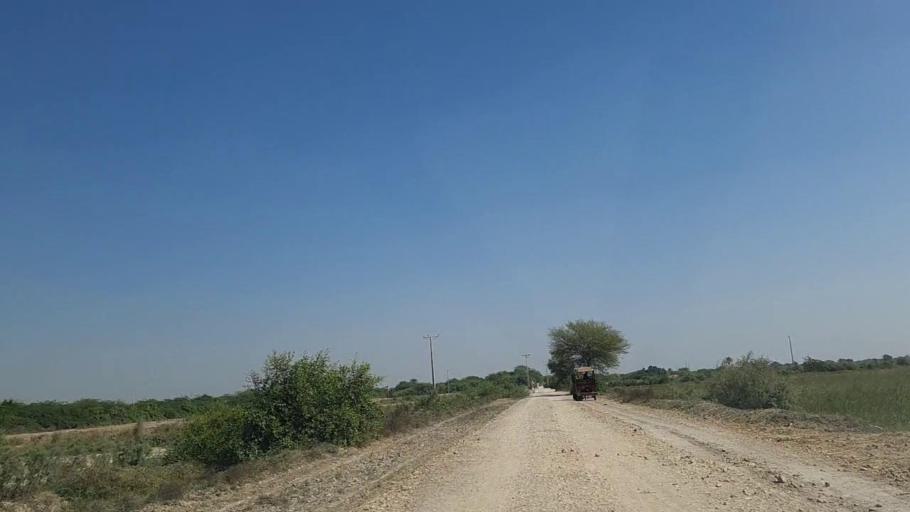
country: PK
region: Sindh
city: Mirpur Batoro
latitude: 24.7323
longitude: 68.2331
